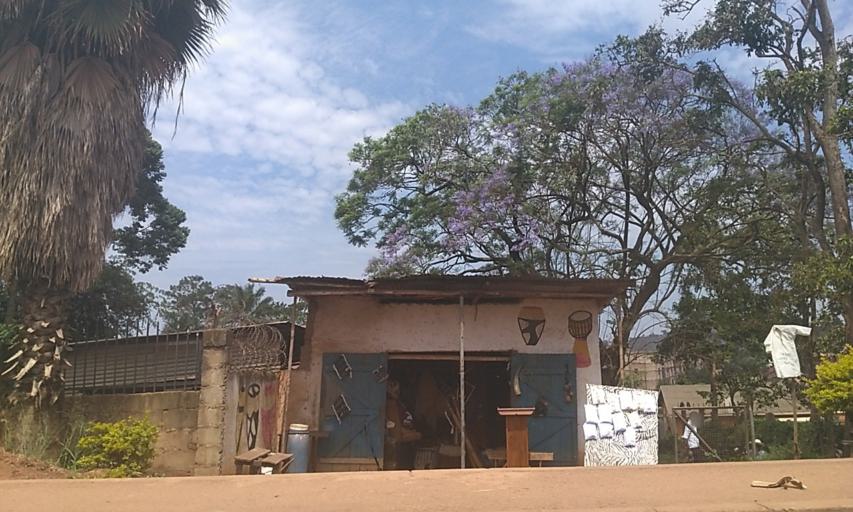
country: UG
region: Central Region
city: Kampala Central Division
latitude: 0.3078
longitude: 32.5539
